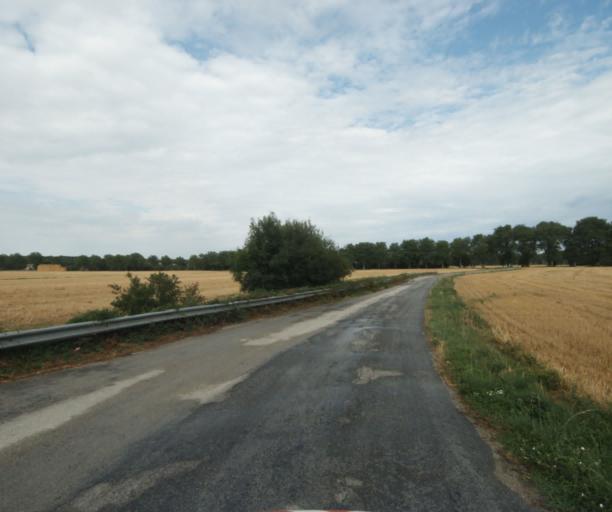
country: FR
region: Midi-Pyrenees
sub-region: Departement de la Haute-Garonne
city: Revel
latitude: 43.4242
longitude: 1.9603
